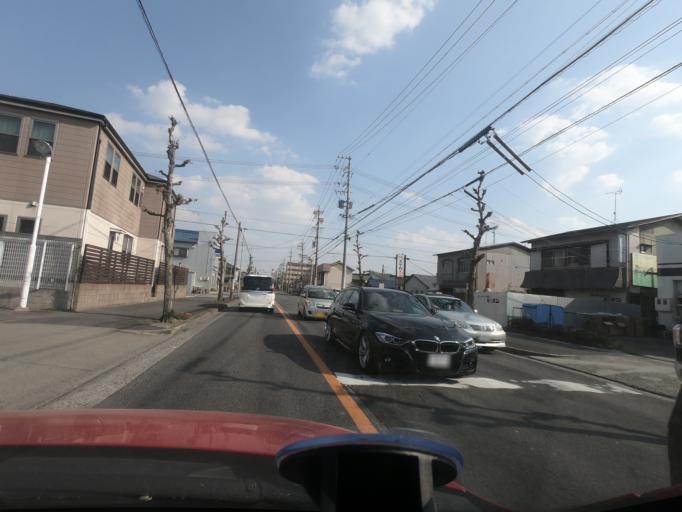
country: JP
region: Aichi
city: Kasugai
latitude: 35.2459
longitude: 136.9629
